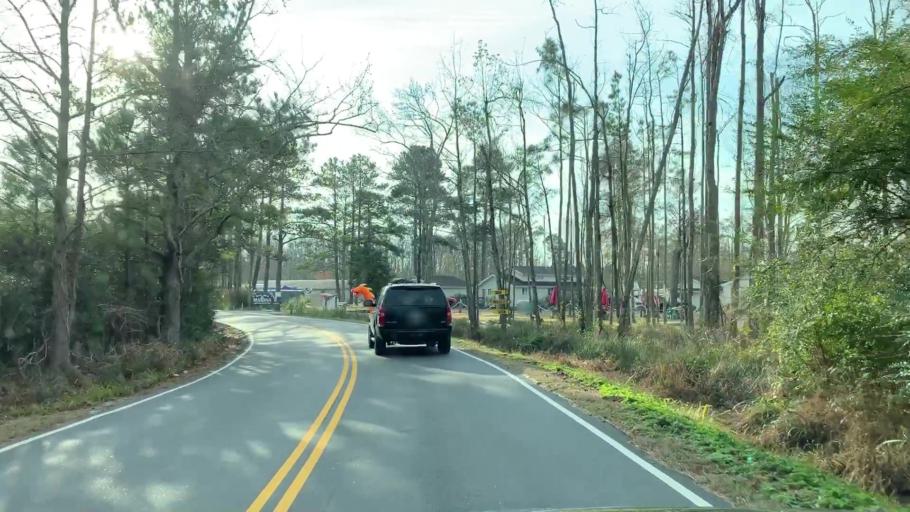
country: US
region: Virginia
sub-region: City of Virginia Beach
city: Virginia Beach
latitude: 36.6928
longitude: -76.0371
